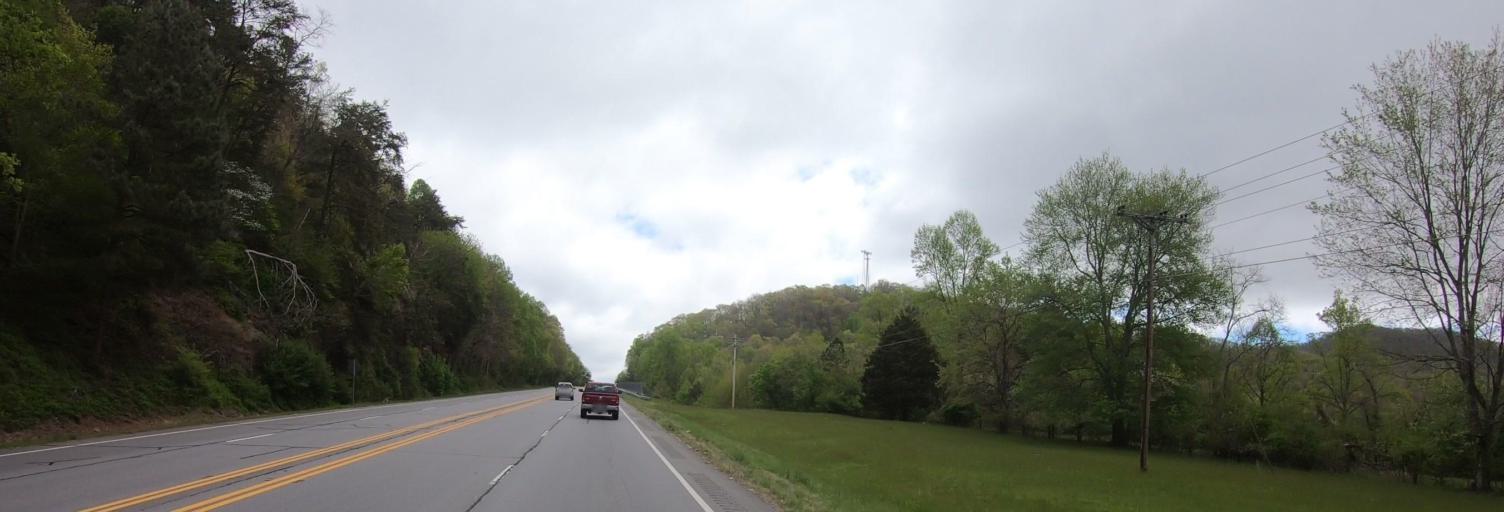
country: US
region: North Carolina
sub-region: Clay County
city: Hayesville
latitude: 34.9650
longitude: -83.8413
